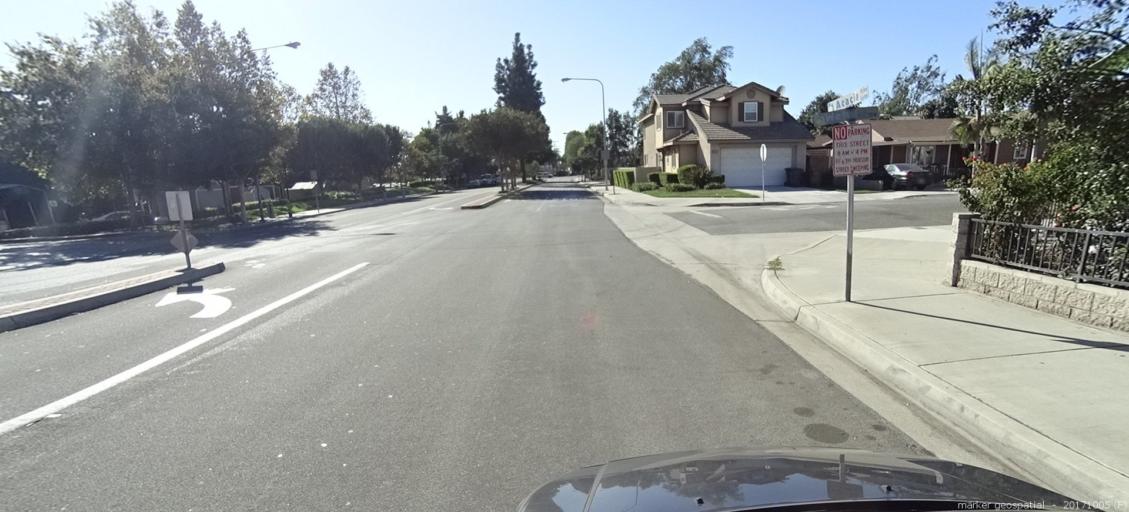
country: US
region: California
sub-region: Orange County
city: Garden Grove
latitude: 33.7760
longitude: -117.9435
